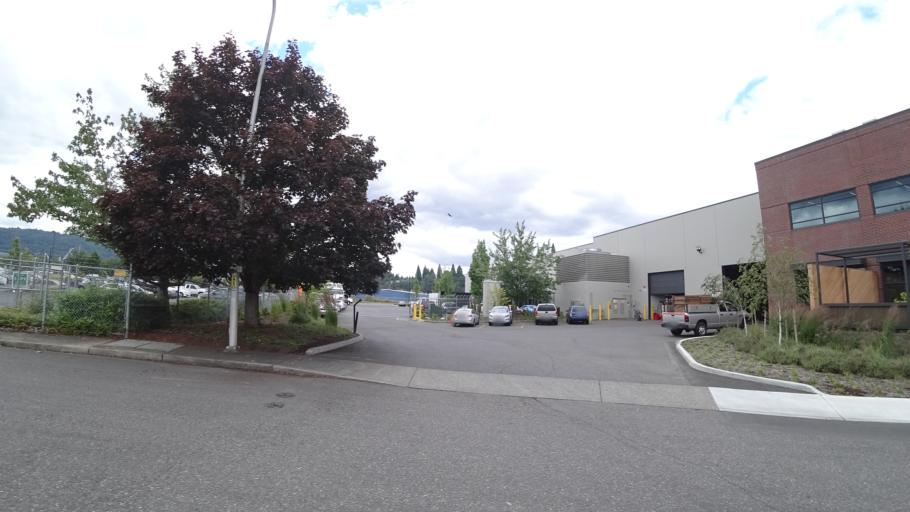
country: US
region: Oregon
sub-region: Multnomah County
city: Portland
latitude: 45.5734
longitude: -122.7106
